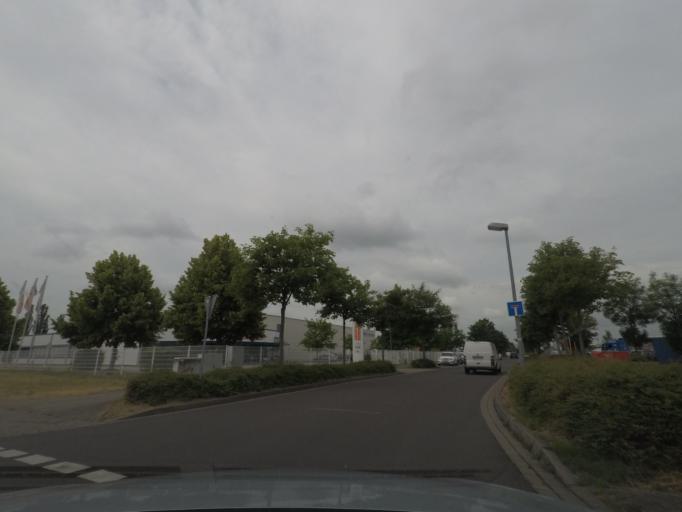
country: DE
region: Saxony-Anhalt
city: Neue Neustadt
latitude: 52.1650
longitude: 11.6076
